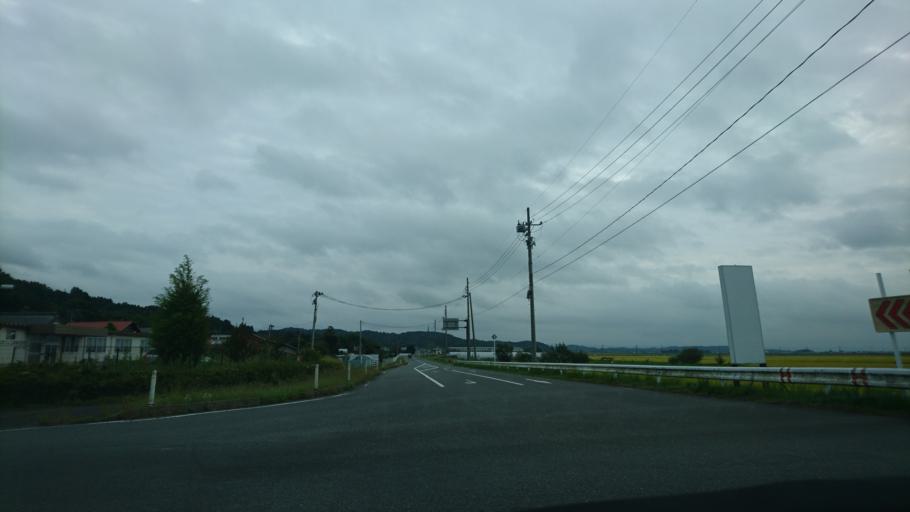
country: JP
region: Iwate
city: Ichinoseki
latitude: 38.8024
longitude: 141.1152
